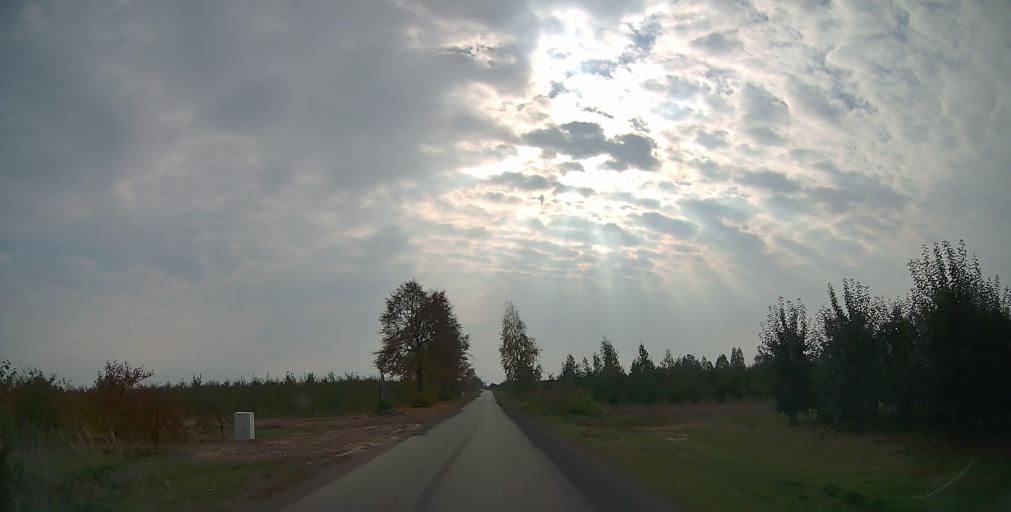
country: PL
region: Masovian Voivodeship
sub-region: Powiat grojecki
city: Mogielnica
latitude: 51.6525
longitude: 20.7242
